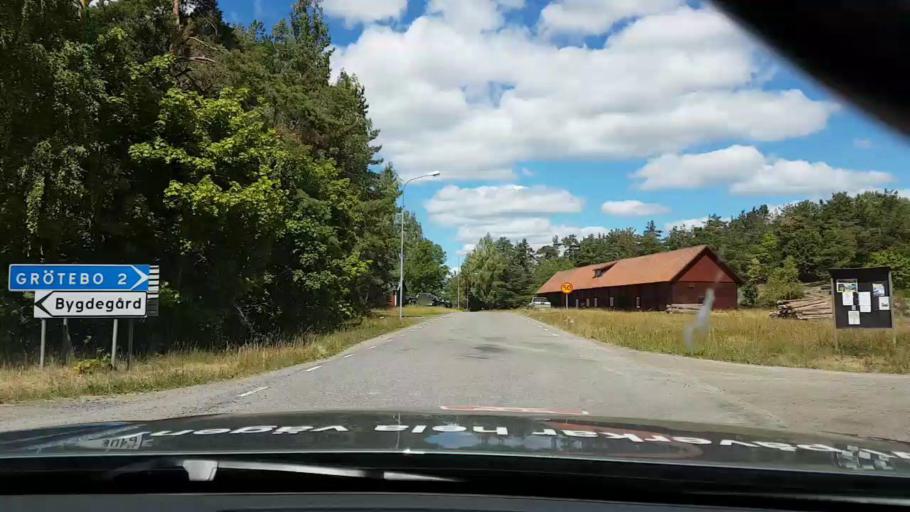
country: SE
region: Kalmar
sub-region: Vasterviks Kommun
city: Forserum
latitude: 58.0114
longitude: 16.5779
